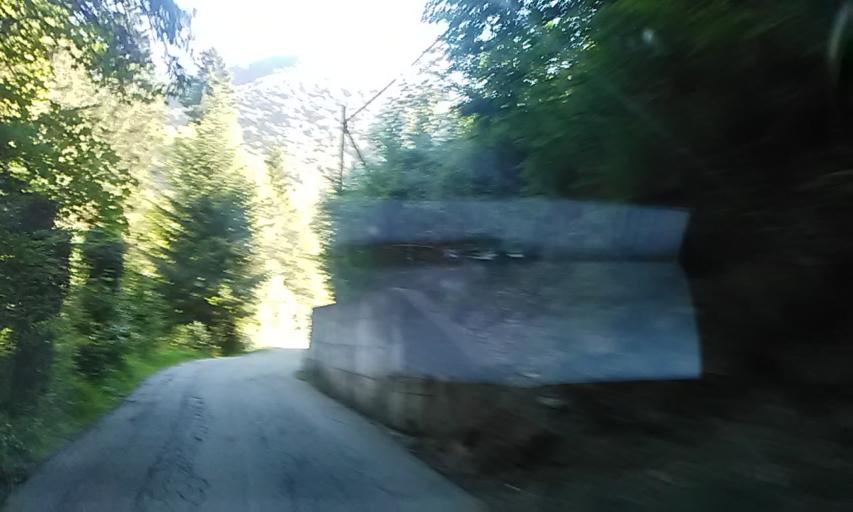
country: IT
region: Piedmont
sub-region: Provincia di Vercelli
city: Varallo
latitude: 45.8267
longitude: 8.2757
